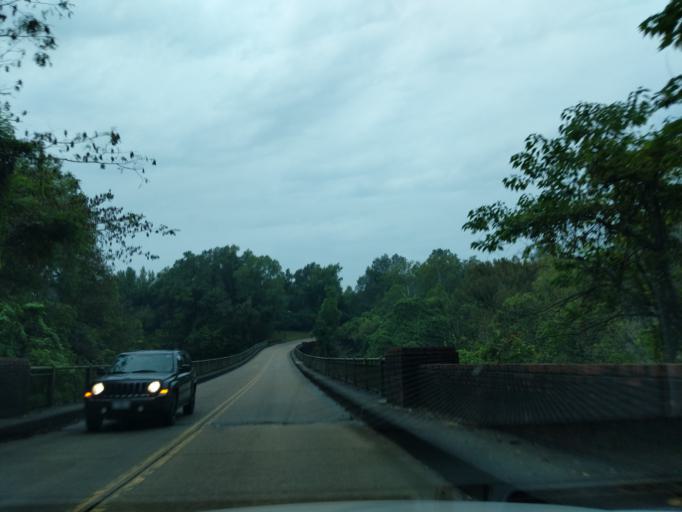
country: US
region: Mississippi
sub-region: Warren County
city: Vicksburg
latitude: 32.3178
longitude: -90.8924
